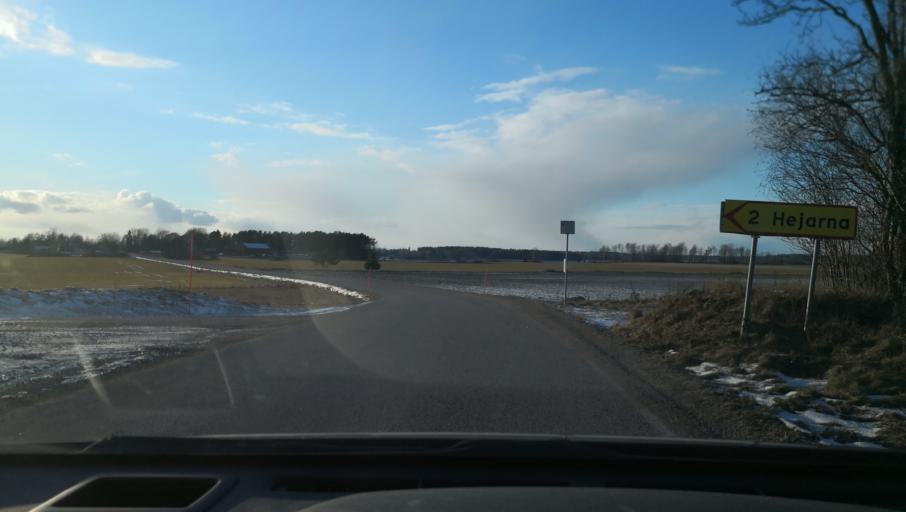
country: SE
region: Vaestmanland
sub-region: Vasteras
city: Tillberga
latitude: 59.6391
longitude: 16.7150
